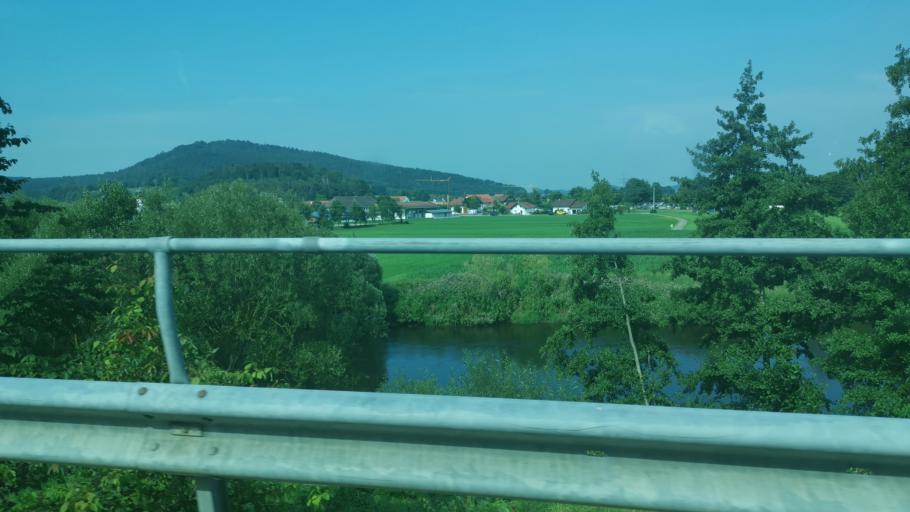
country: DE
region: Bavaria
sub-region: Upper Palatinate
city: Chamerau
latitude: 49.1992
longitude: 12.7523
